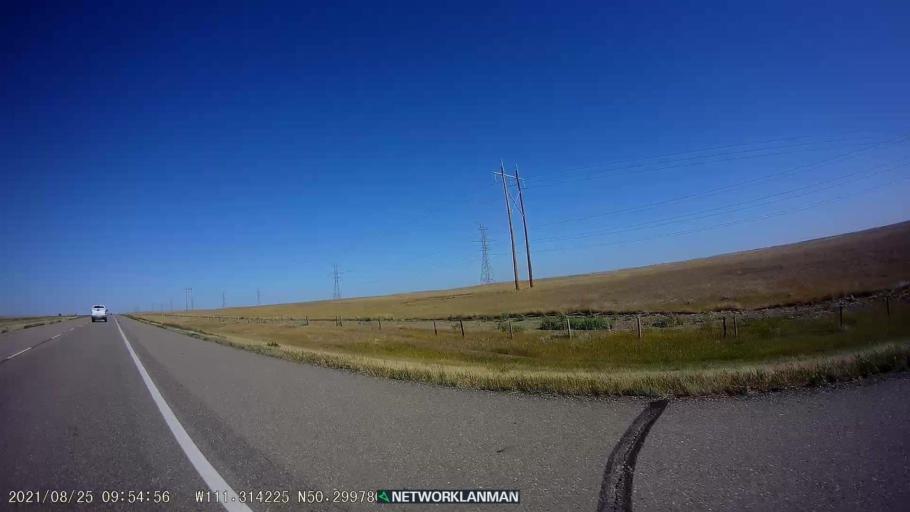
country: CA
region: Alberta
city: Bow Island
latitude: 50.3002
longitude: -111.3149
